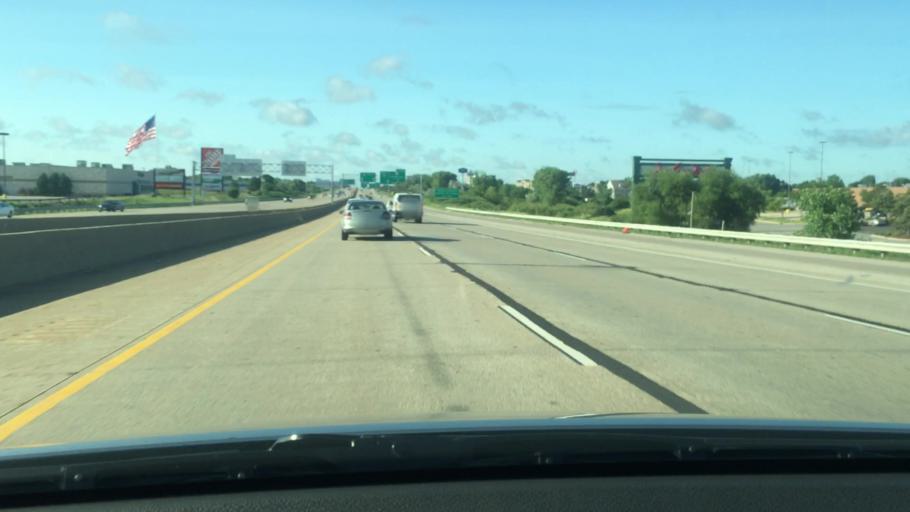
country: US
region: Wisconsin
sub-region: Outagamie County
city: Appleton
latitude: 44.2710
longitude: -88.4664
